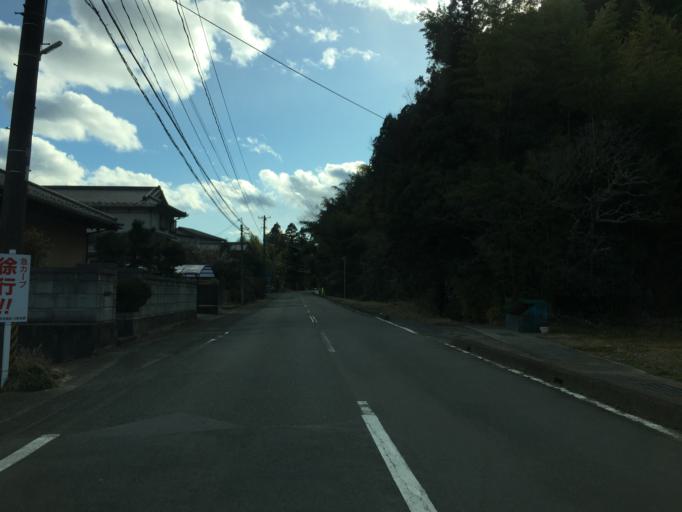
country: JP
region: Ibaraki
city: Kitaibaraki
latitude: 36.9206
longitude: 140.7387
